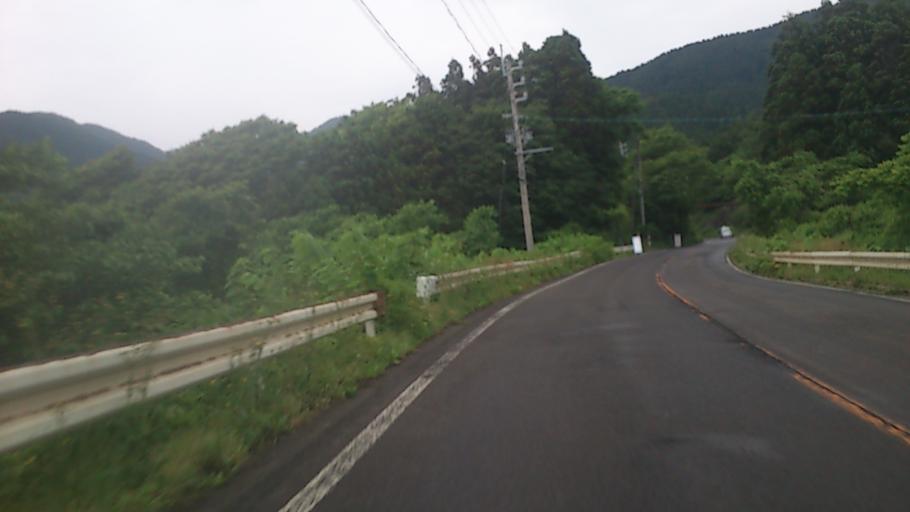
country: JP
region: Akita
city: Noshiromachi
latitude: 40.3959
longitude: 139.9827
